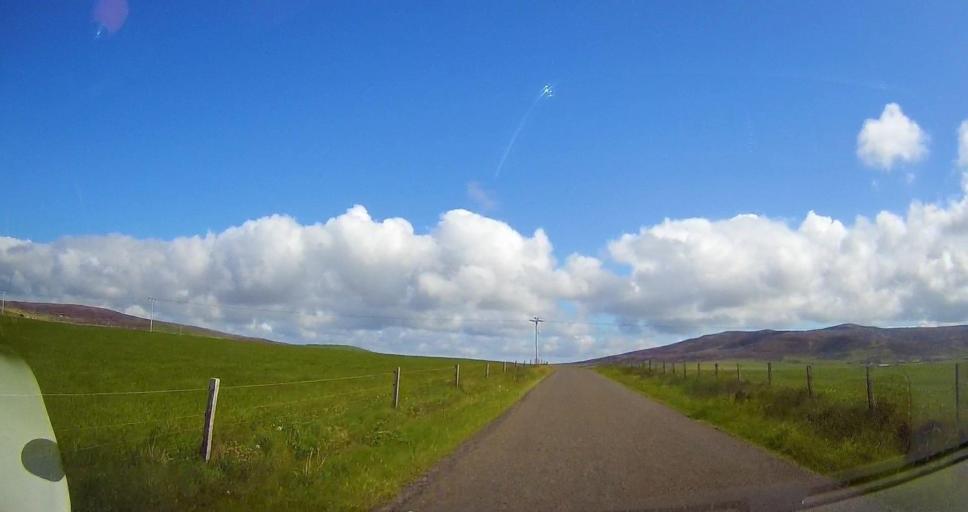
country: GB
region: Scotland
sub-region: Orkney Islands
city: Stromness
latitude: 58.9904
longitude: -3.1554
